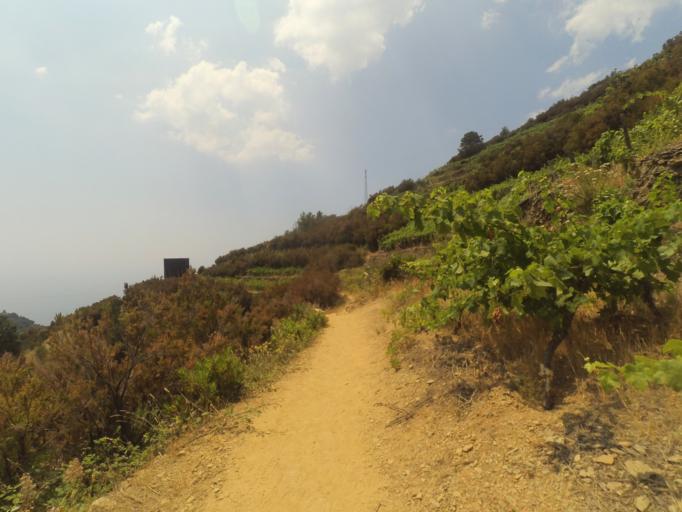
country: IT
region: Liguria
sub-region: Provincia di La Spezia
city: Riomaggiore
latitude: 44.1102
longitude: 9.7320
